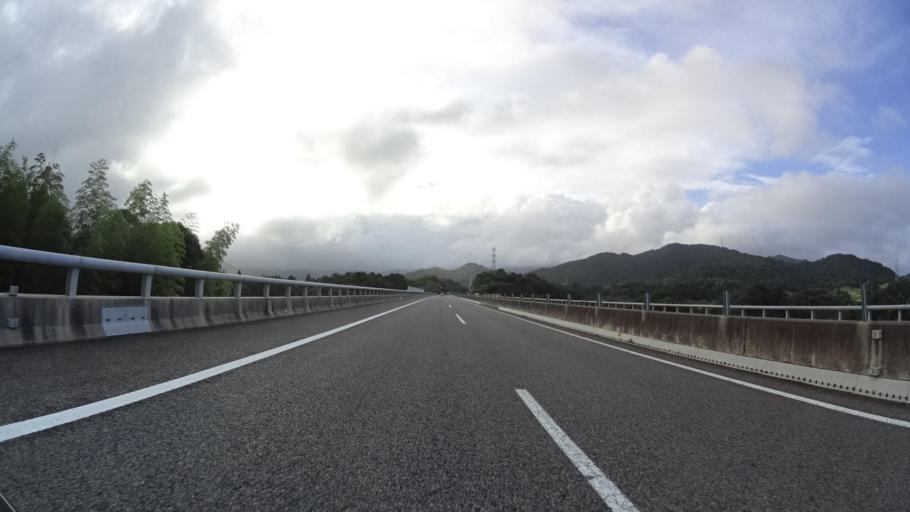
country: JP
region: Mie
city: Kameyama
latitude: 34.9047
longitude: 136.4375
